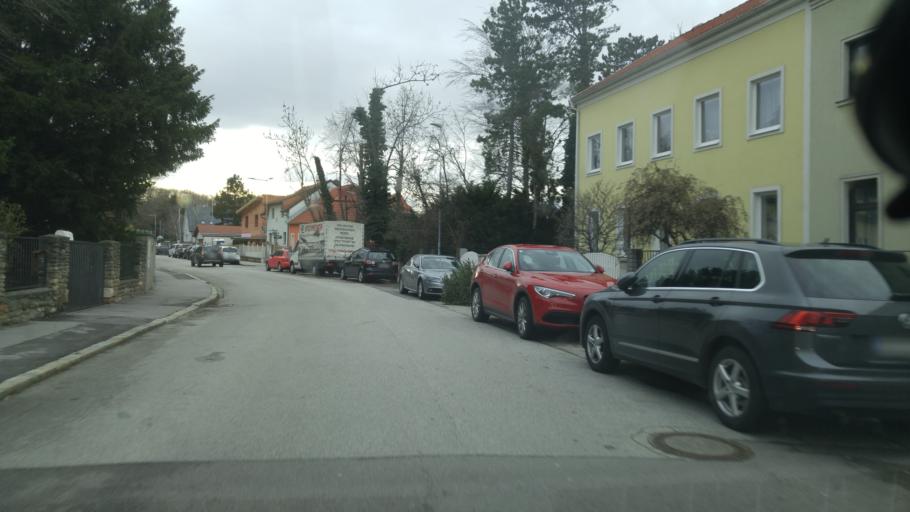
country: AT
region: Lower Austria
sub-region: Politischer Bezirk Wien-Umgebung
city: Himberg
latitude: 48.0837
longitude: 16.4366
